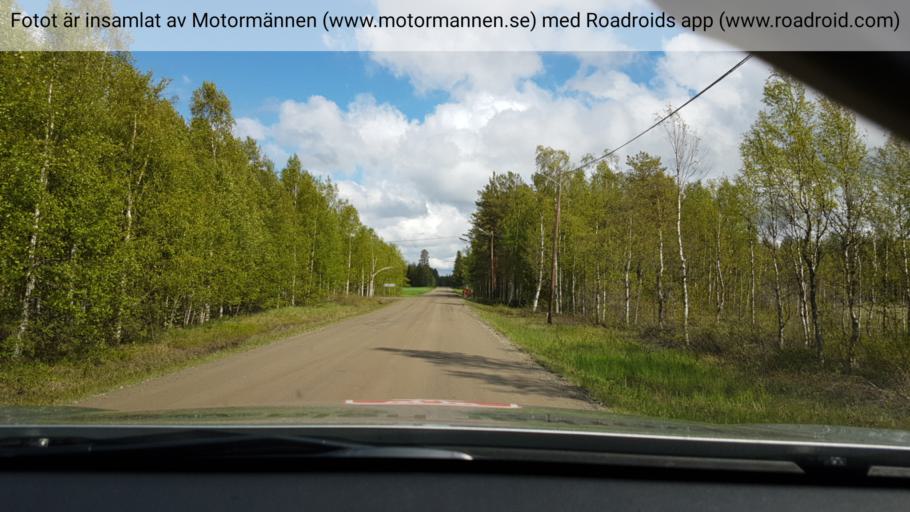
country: SE
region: Vaesterbotten
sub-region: Vindelns Kommun
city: Vindeln
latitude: 64.0794
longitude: 19.6121
